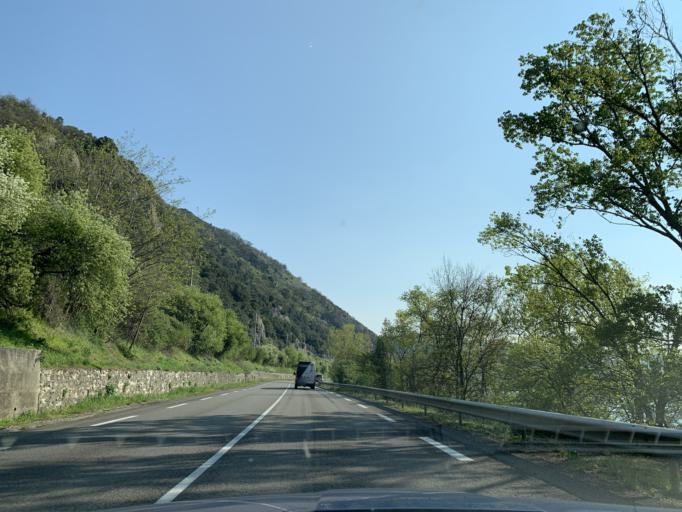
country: FR
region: Rhone-Alpes
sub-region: Departement de l'Ardeche
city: Saint-Jean-de-Muzols
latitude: 45.0884
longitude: 4.8333
